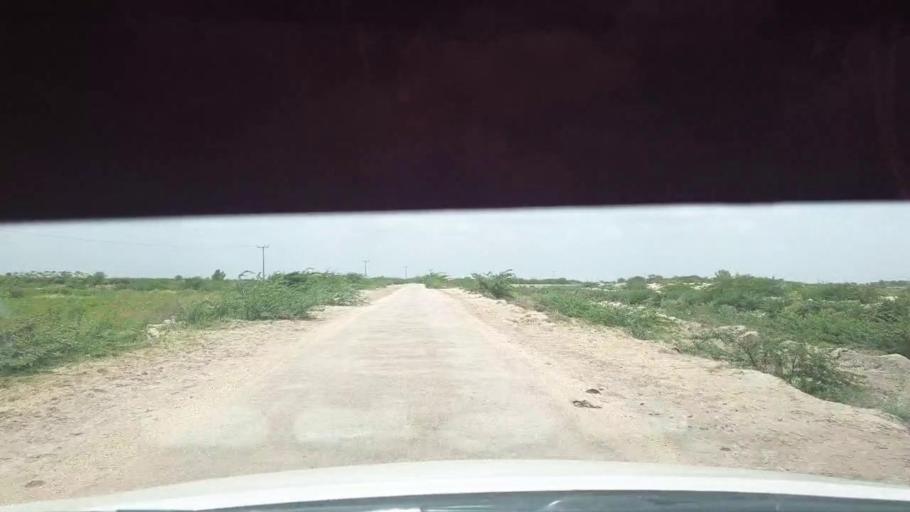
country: PK
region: Sindh
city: Kadhan
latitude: 24.4854
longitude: 69.0670
